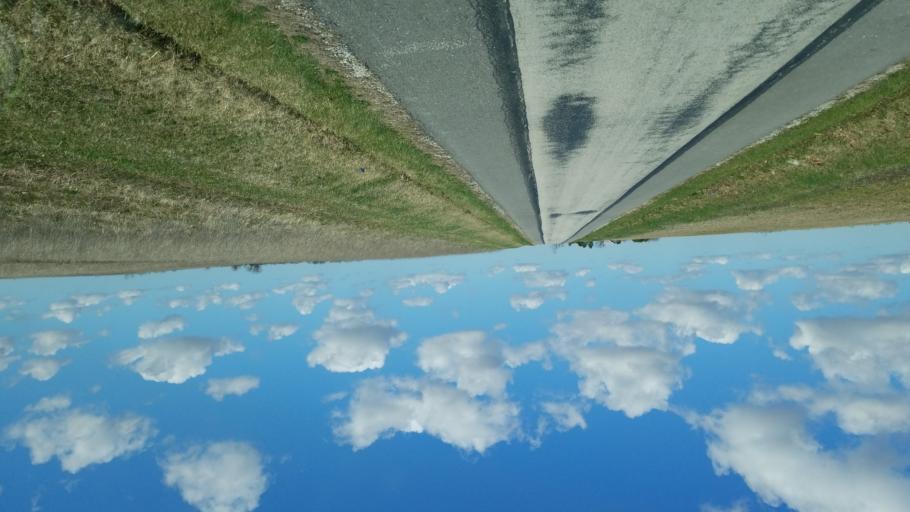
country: US
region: Ohio
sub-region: Sandusky County
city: Mount Carmel
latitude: 41.0891
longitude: -82.9382
